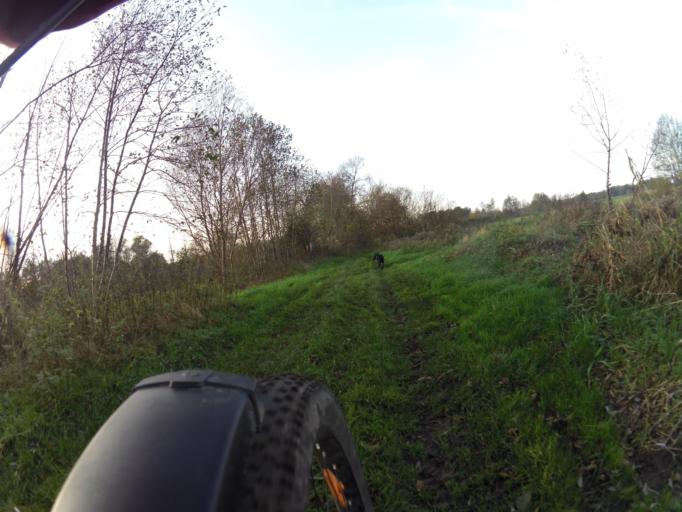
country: PL
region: Pomeranian Voivodeship
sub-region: Powiat pucki
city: Krokowa
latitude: 54.7750
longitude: 18.1699
